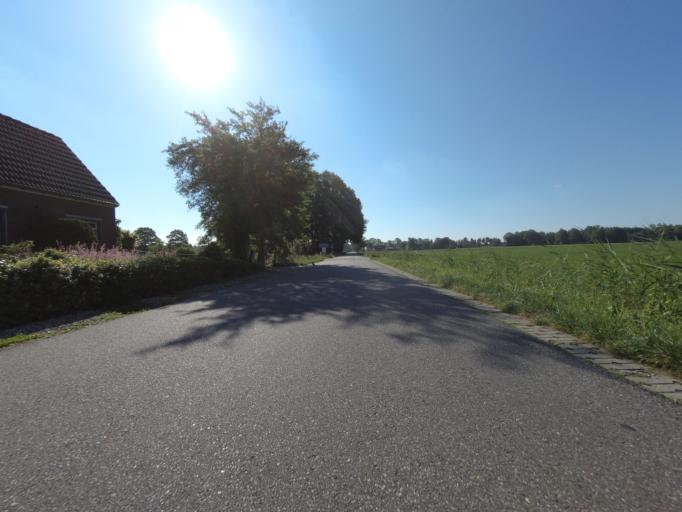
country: NL
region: Gelderland
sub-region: Gemeente Brummen
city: Eerbeek
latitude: 52.1637
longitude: 6.0600
